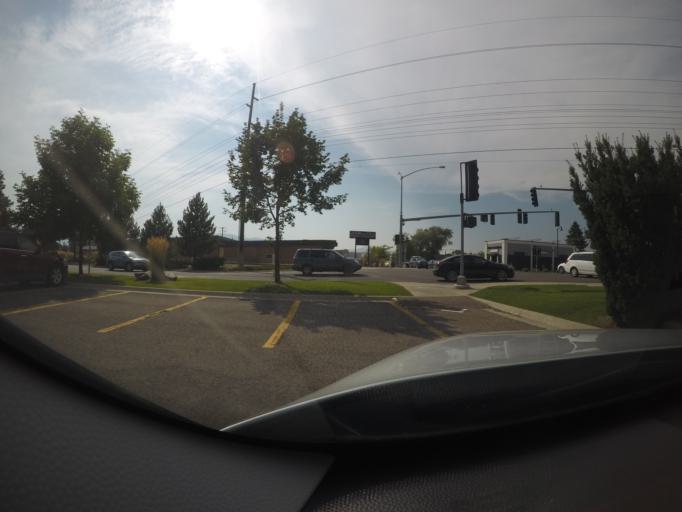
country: US
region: Montana
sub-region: Missoula County
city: Orchard Homes
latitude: 46.8486
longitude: -114.0277
